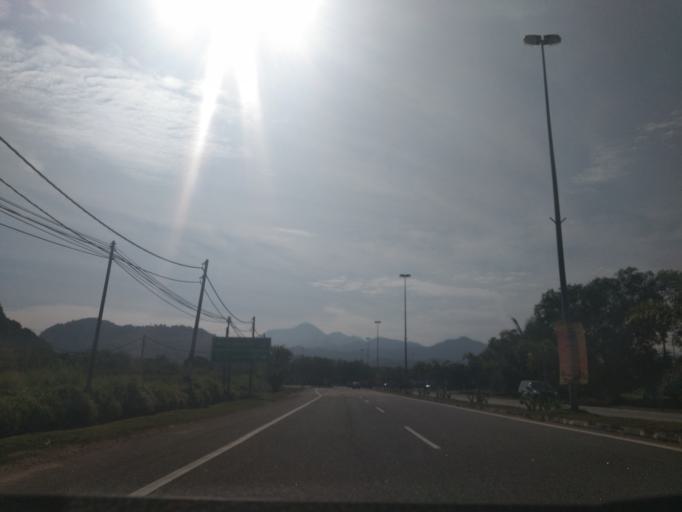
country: MY
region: Perak
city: Ipoh
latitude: 4.5021
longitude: 101.1450
